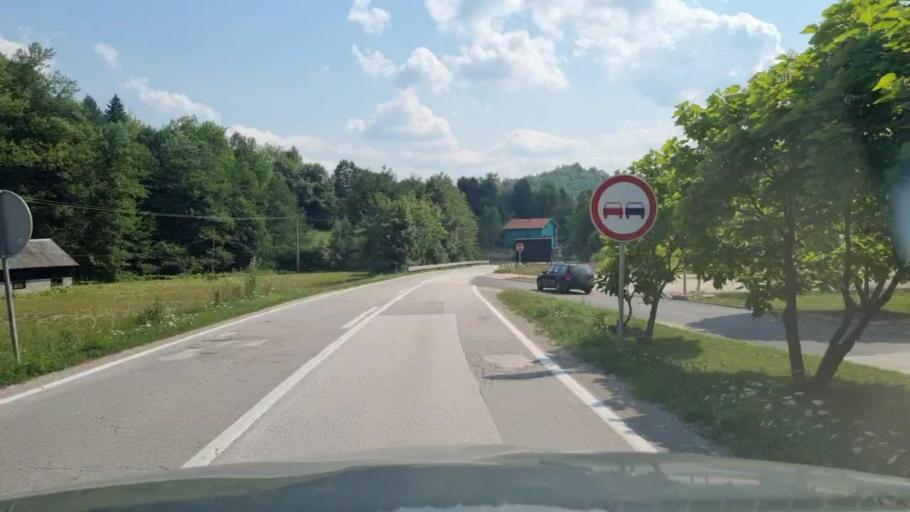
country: BA
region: Federation of Bosnia and Herzegovina
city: Olovo
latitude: 44.1591
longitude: 18.6387
